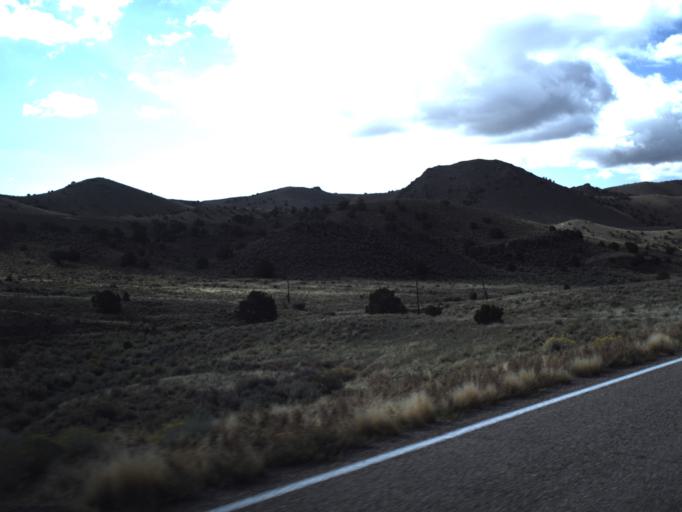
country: US
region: Utah
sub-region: Beaver County
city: Milford
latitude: 38.4490
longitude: -113.2606
